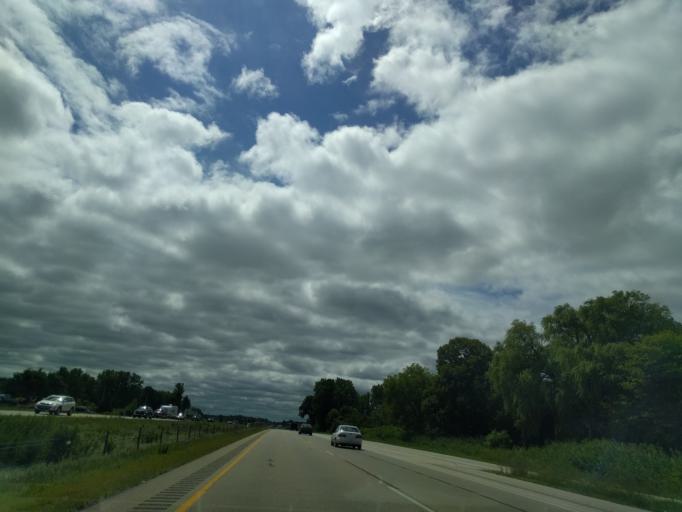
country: US
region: Wisconsin
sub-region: Brown County
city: Suamico
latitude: 44.6747
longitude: -88.0504
